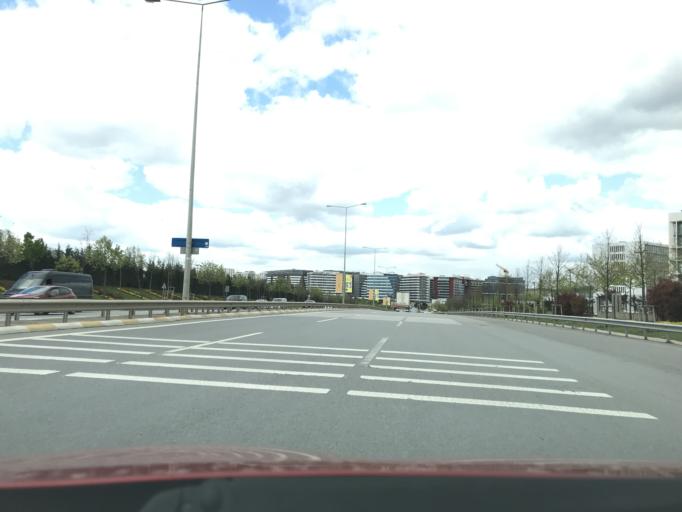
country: TR
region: Istanbul
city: Sultanbeyli
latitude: 40.9203
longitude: 29.3123
